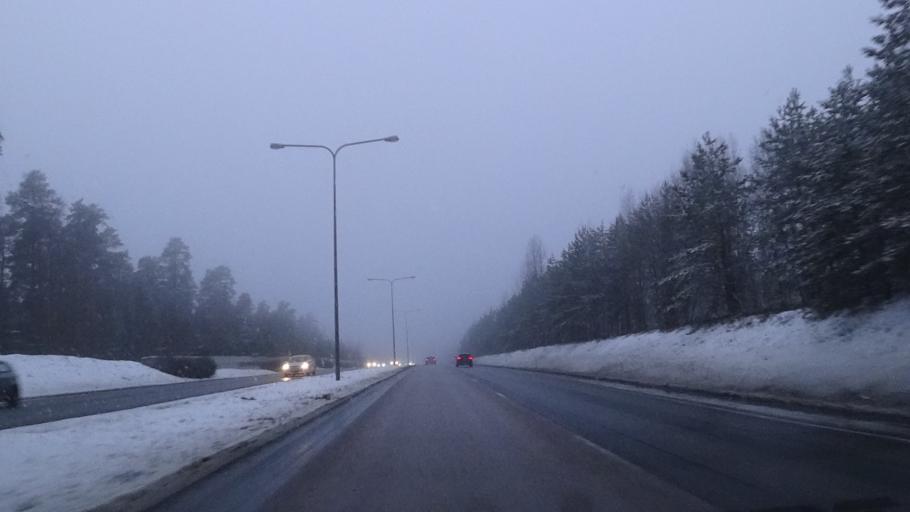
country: FI
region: Paijanne Tavastia
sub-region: Lahti
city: Hollola
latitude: 60.9869
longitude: 25.5318
